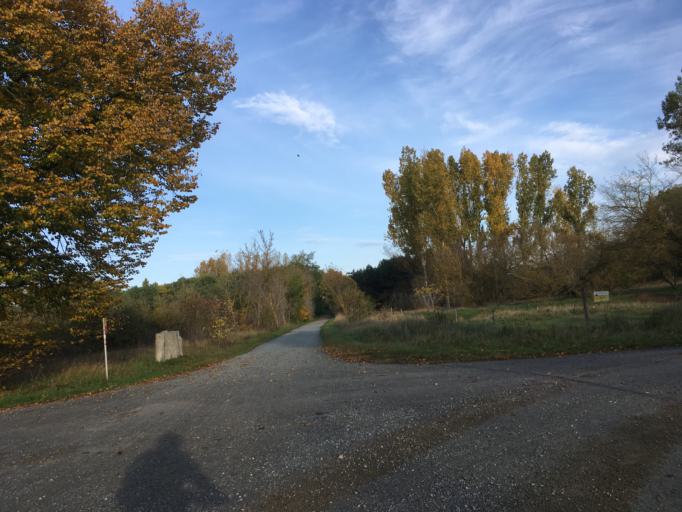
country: DE
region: Berlin
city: Buch
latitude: 52.6695
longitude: 13.4851
